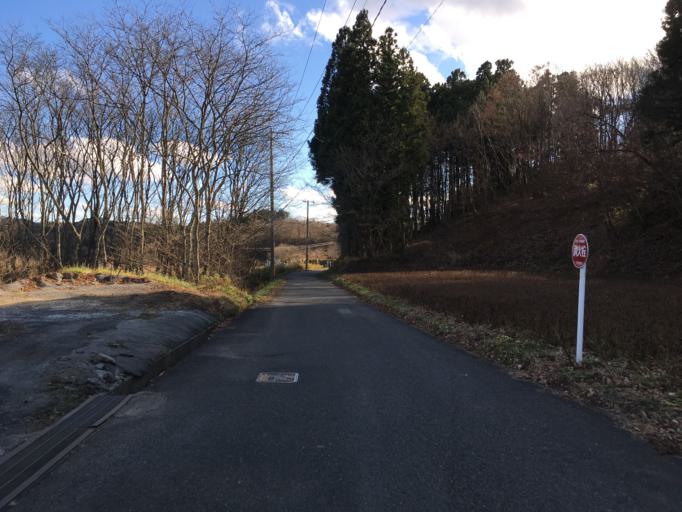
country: JP
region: Fukushima
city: Ishikawa
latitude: 37.2627
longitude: 140.5595
